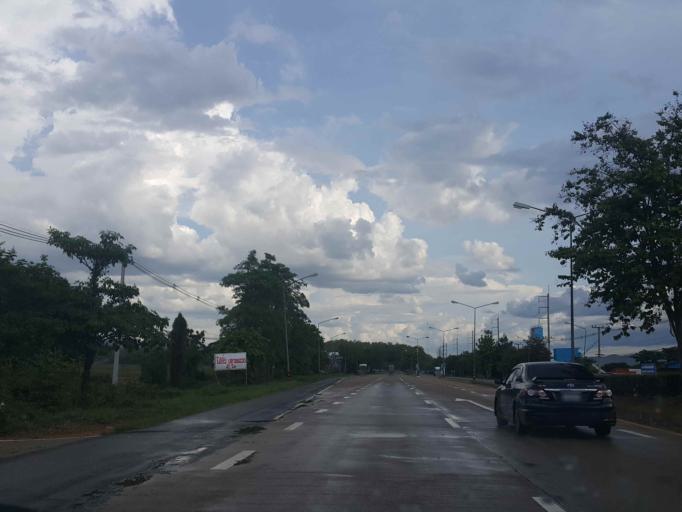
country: TH
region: Phrae
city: Den Chai
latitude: 17.9945
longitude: 100.0992
